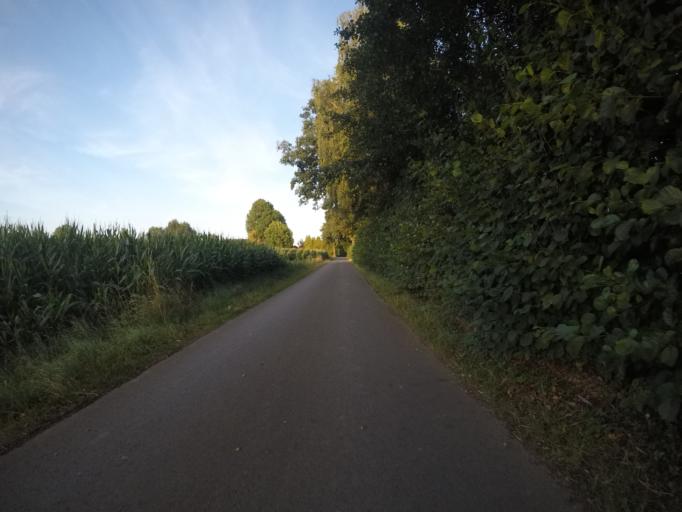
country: DE
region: North Rhine-Westphalia
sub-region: Regierungsbezirk Munster
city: Isselburg
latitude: 51.8548
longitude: 6.5150
